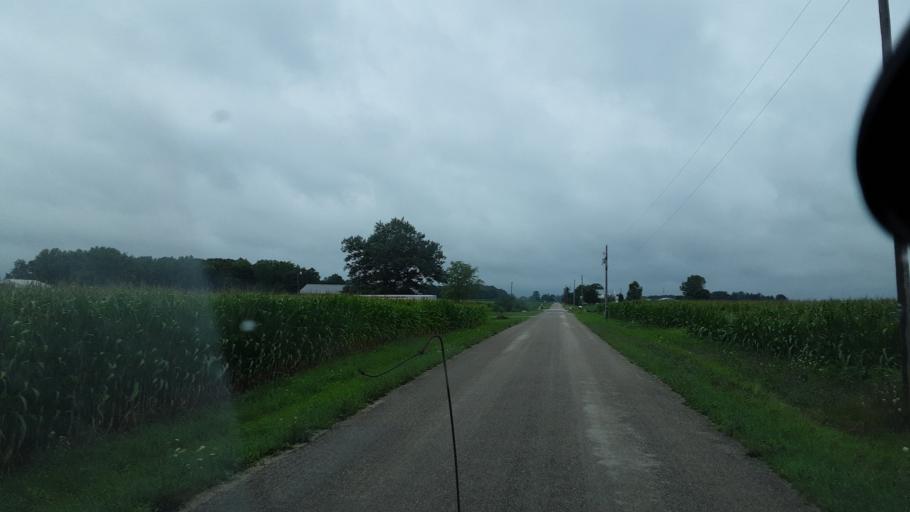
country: US
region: Indiana
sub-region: Adams County
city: Decatur
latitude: 40.8345
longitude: -84.8121
